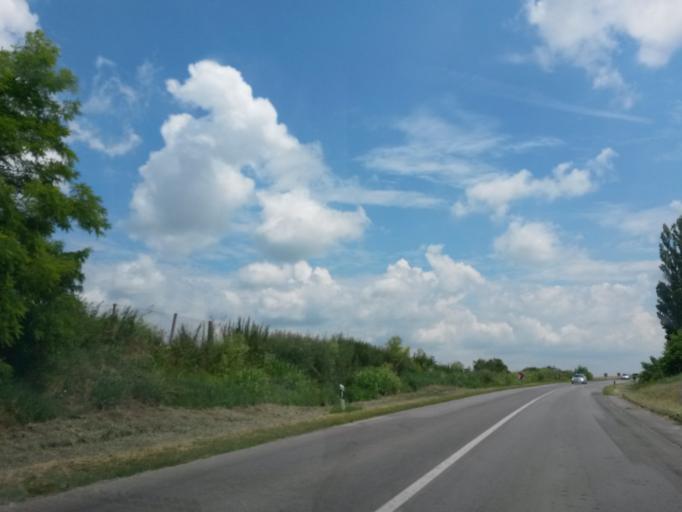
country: HR
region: Osjecko-Baranjska
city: Sarvas
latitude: 45.5182
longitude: 18.9128
